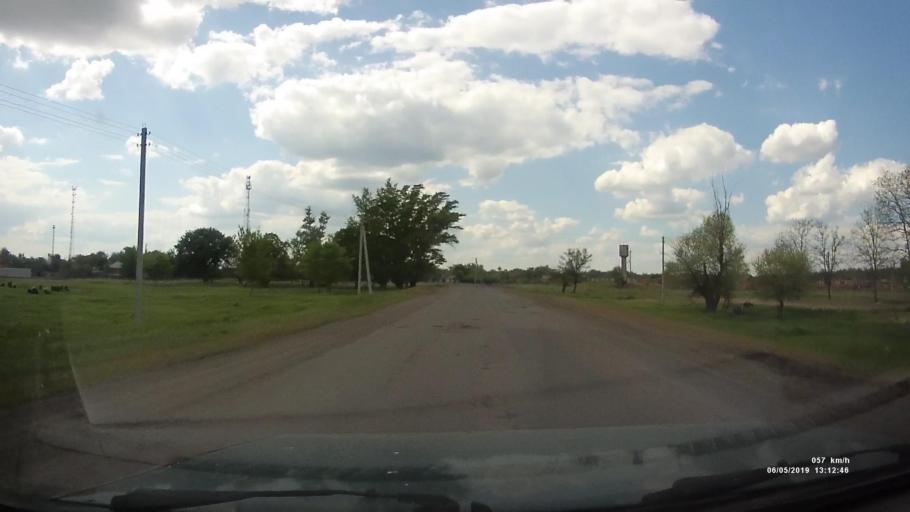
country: RU
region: Rostov
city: Ust'-Donetskiy
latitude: 47.7555
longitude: 40.9427
